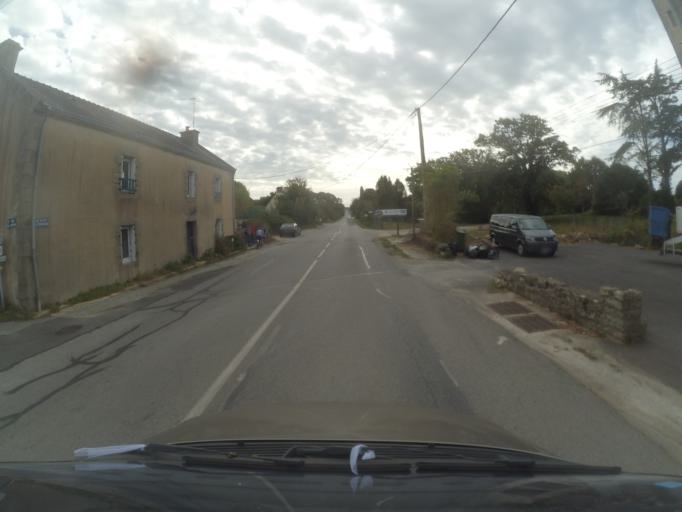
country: FR
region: Brittany
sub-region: Departement du Morbihan
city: Belz
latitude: 47.6592
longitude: -3.1720
